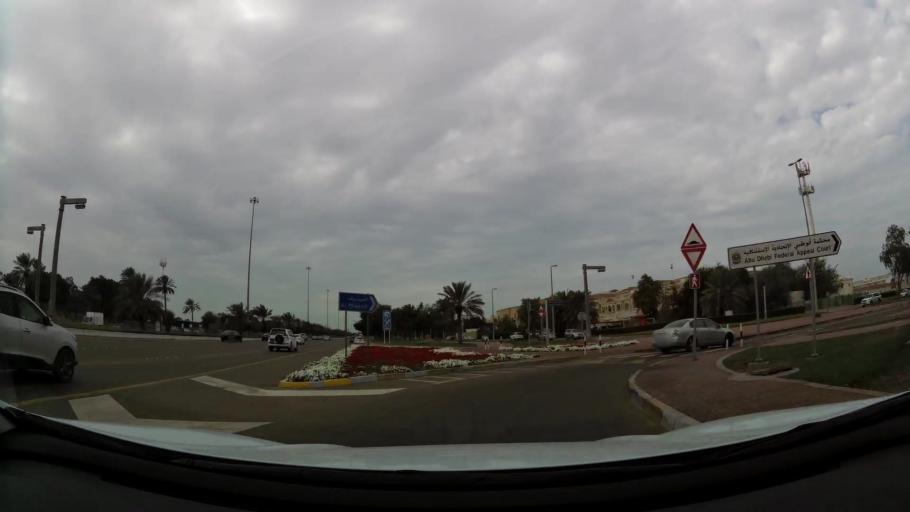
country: AE
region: Abu Dhabi
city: Abu Dhabi
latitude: 24.4274
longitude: 54.4005
